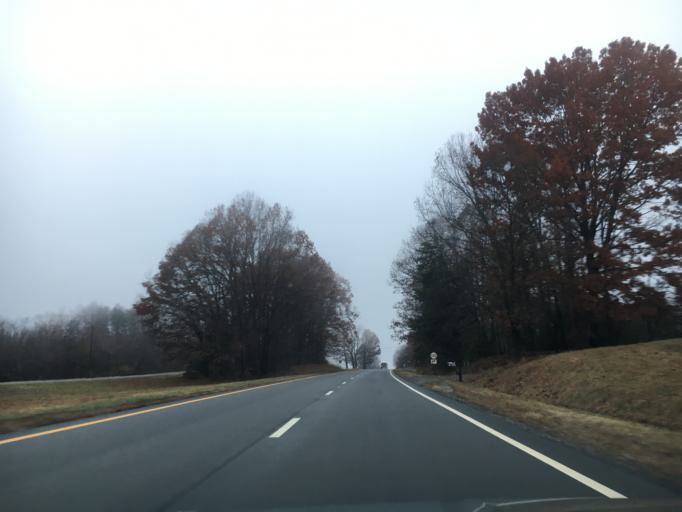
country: US
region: Virginia
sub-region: Prince Edward County
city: Hampden Sydney
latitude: 37.3051
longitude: -78.5259
